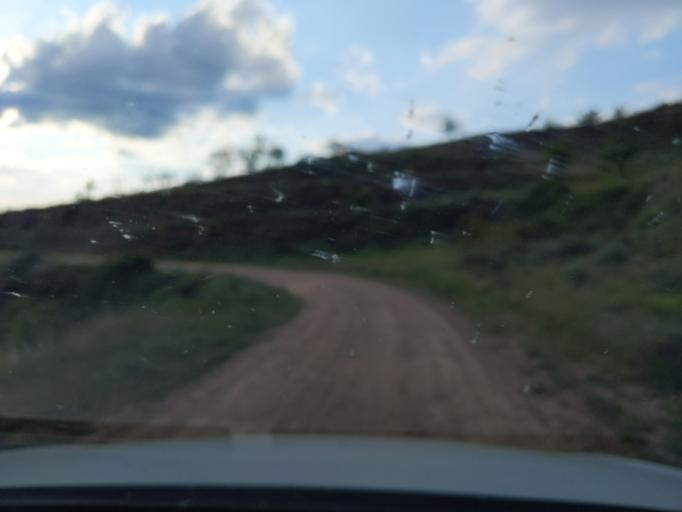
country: ES
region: La Rioja
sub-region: Provincia de La Rioja
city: Nalda
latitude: 42.3269
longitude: -2.4742
